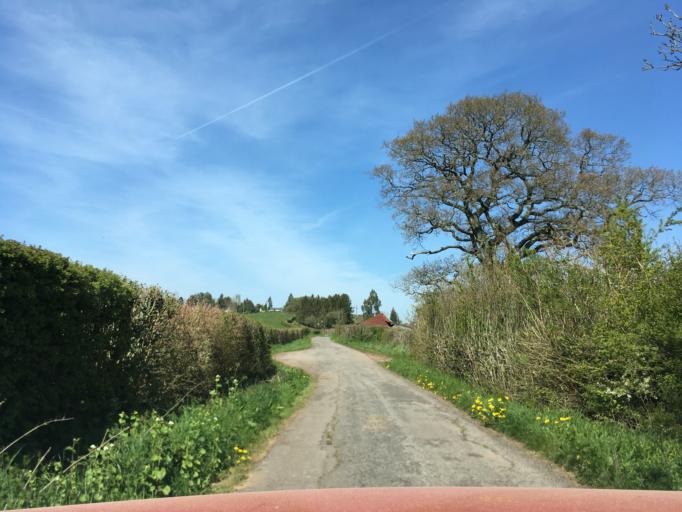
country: GB
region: Wales
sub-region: Monmouthshire
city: Llangwm
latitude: 51.7400
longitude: -2.8244
